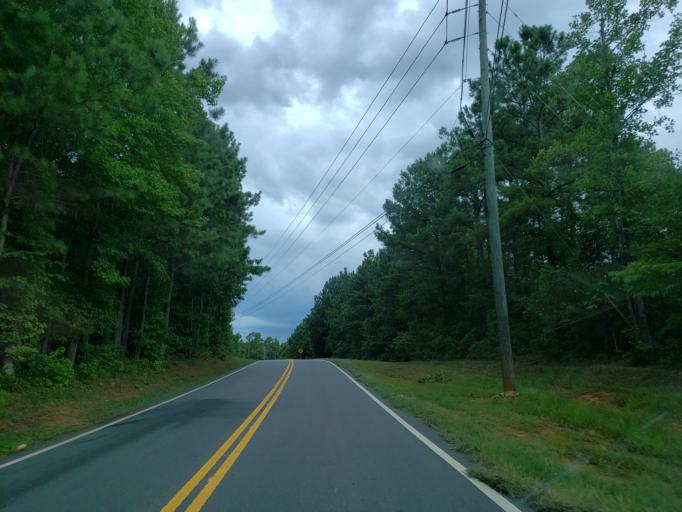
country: US
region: Georgia
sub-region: Paulding County
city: Dallas
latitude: 33.9930
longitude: -84.7950
